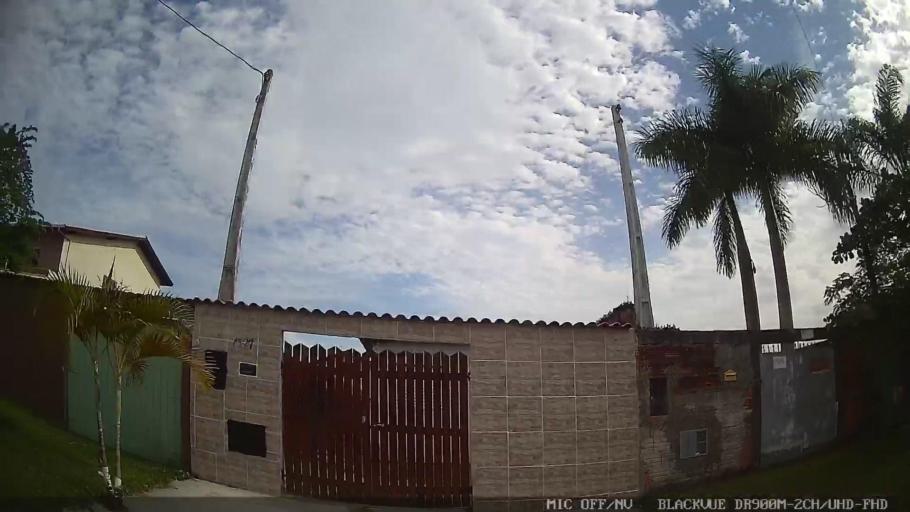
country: BR
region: Sao Paulo
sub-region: Itanhaem
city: Itanhaem
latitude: -24.1568
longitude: -46.7715
